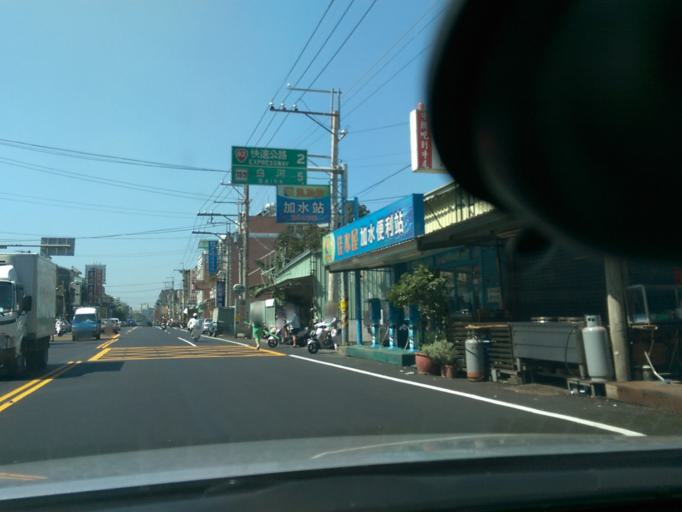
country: TW
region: Taiwan
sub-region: Chiayi
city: Jiayi Shi
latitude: 23.4492
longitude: 120.4592
